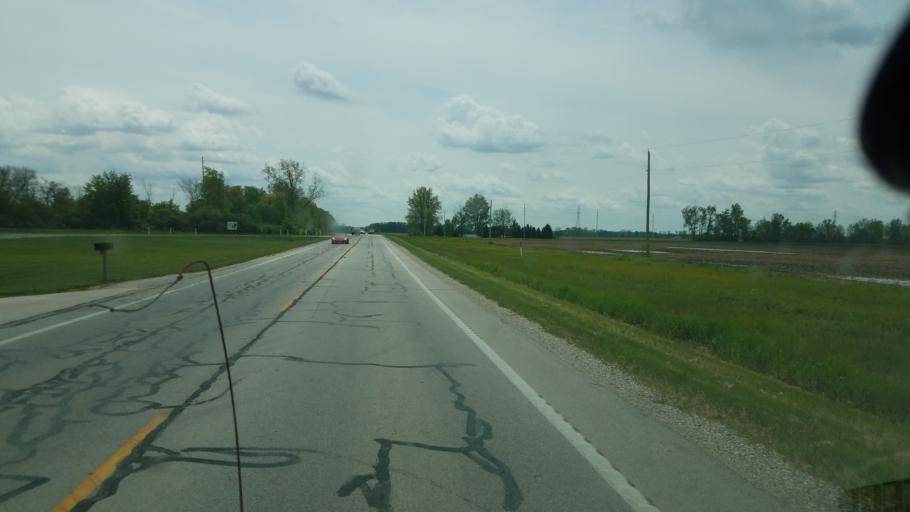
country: US
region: Ohio
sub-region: Sandusky County
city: Stony Prairie
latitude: 41.3236
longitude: -83.1682
